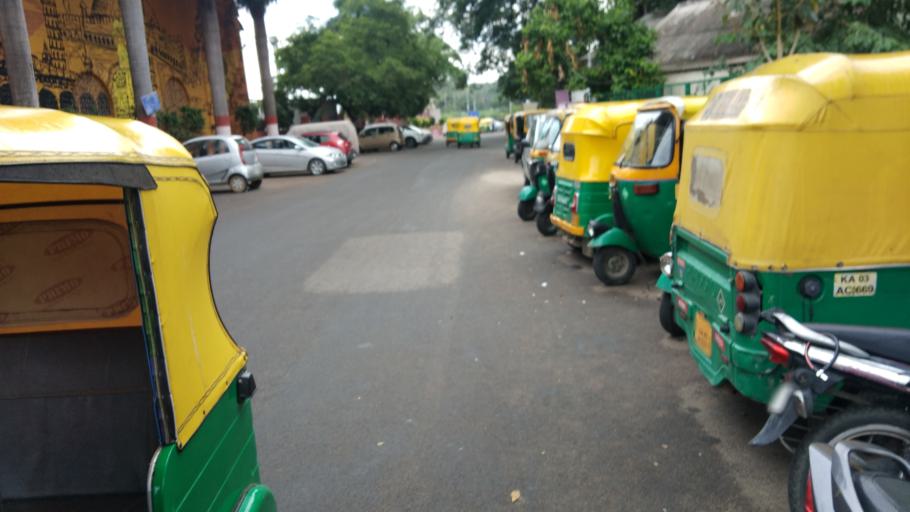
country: IN
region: Karnataka
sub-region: Bangalore Urban
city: Bangalore
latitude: 12.9942
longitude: 77.5979
